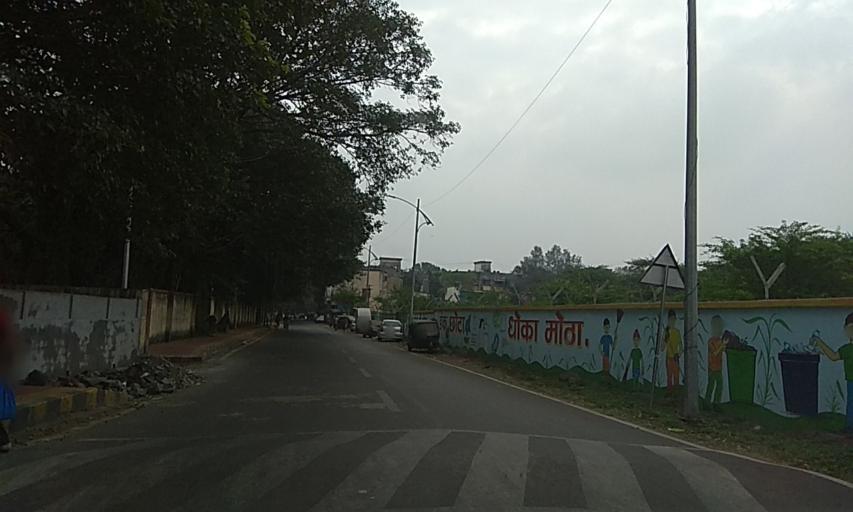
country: IN
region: Maharashtra
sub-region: Pune Division
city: Khadki
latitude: 18.5527
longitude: 73.8538
